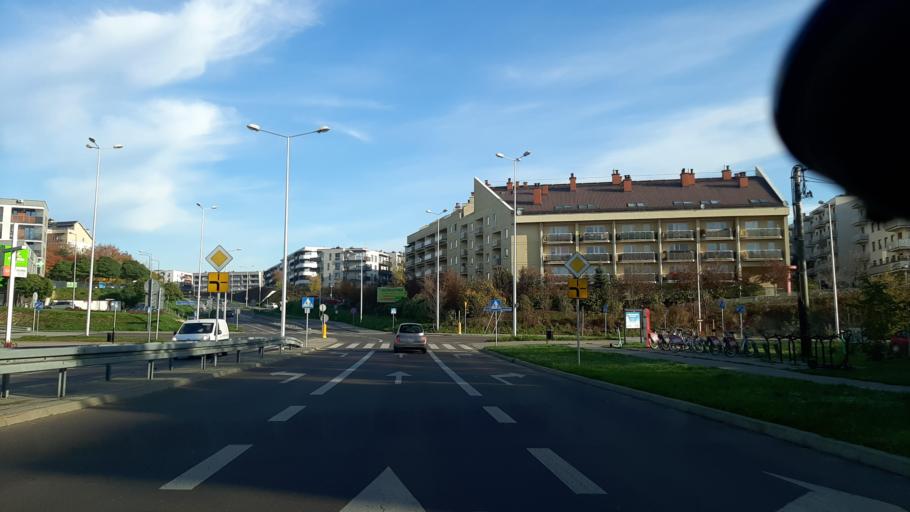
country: PL
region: Lublin Voivodeship
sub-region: Powiat lubelski
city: Lublin
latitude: 51.2691
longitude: 22.5823
